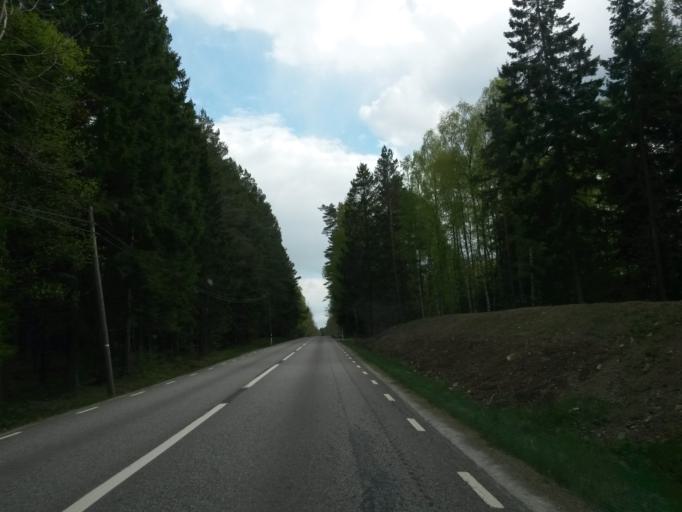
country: SE
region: Vaestra Goetaland
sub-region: Vargarda Kommun
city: Vargarda
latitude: 57.9357
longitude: 12.8524
